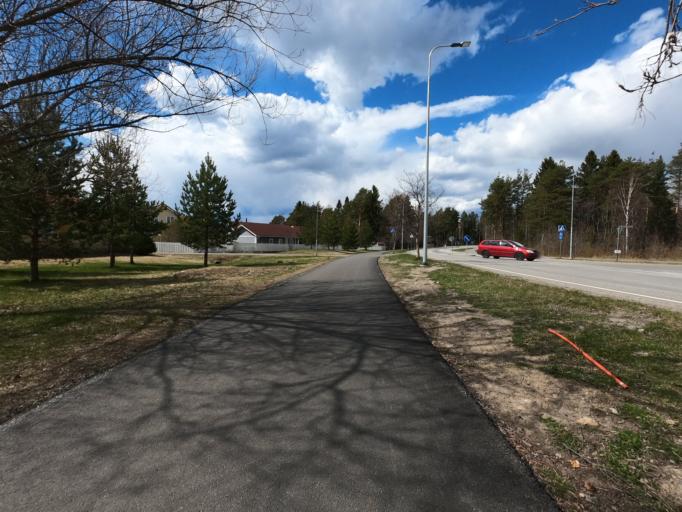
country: FI
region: North Karelia
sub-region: Joensuu
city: Joensuu
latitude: 62.5806
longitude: 29.7699
